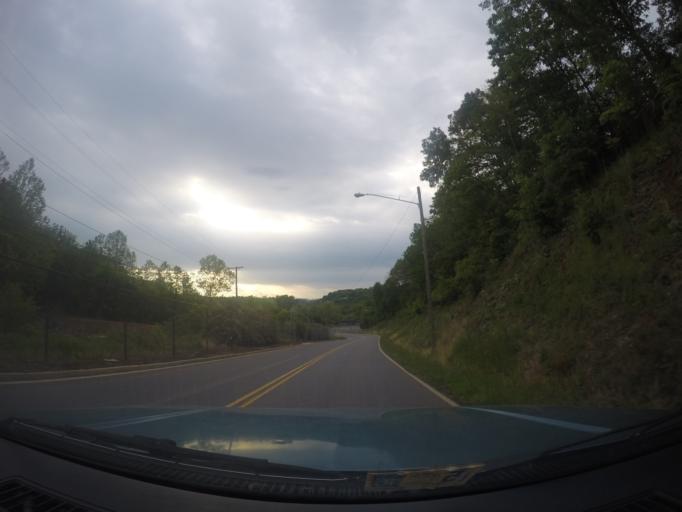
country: US
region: Virginia
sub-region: City of Lynchburg
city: Lynchburg
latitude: 37.3960
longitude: -79.1100
